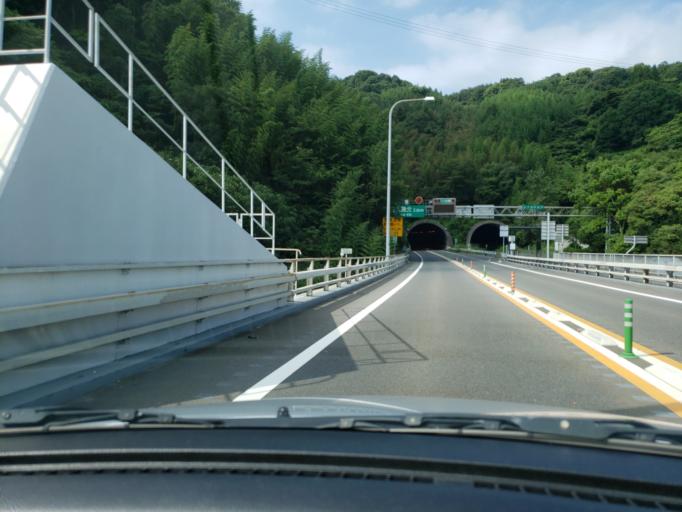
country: JP
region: Hiroshima
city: Innoshima
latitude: 34.1893
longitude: 133.0701
